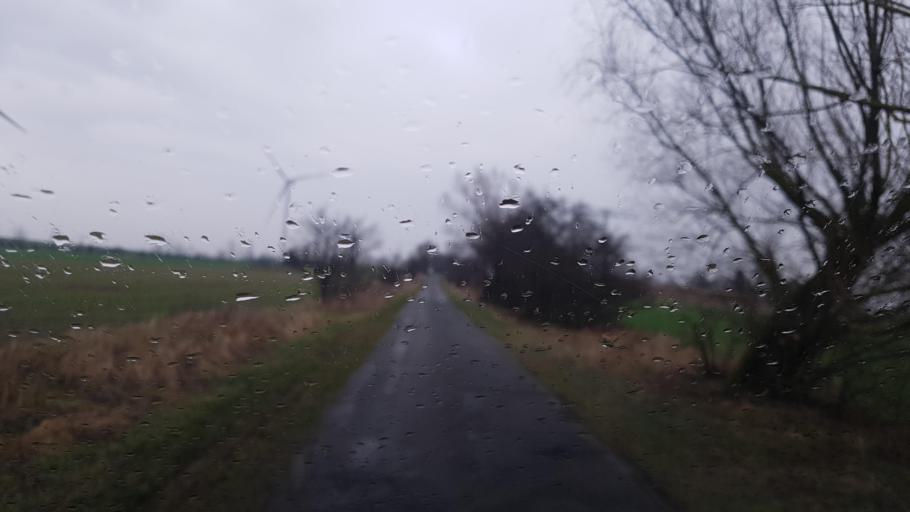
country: DE
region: Brandenburg
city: Zehdenick
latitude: 52.9561
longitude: 13.2568
